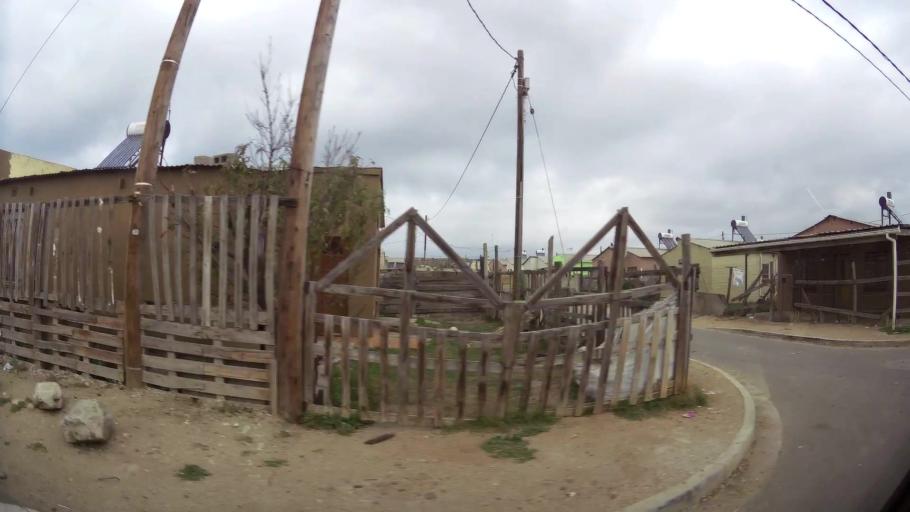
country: ZA
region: Eastern Cape
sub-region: Nelson Mandela Bay Metropolitan Municipality
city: Port Elizabeth
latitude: -33.8882
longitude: 25.6044
